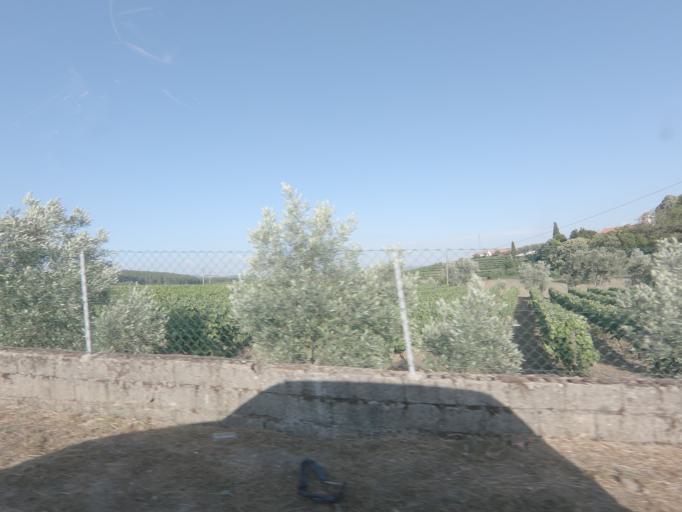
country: PT
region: Vila Real
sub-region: Sabrosa
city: Sabrosa
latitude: 41.2580
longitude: -7.5960
